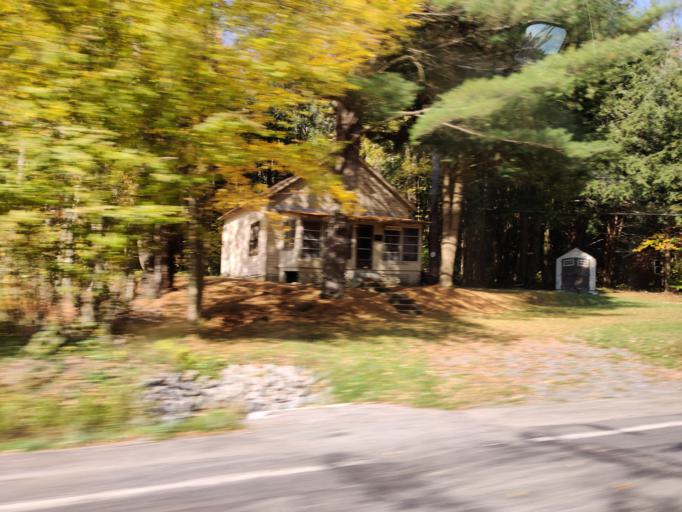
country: US
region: Pennsylvania
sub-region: Warren County
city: Sheffield
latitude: 41.5809
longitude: -79.0447
